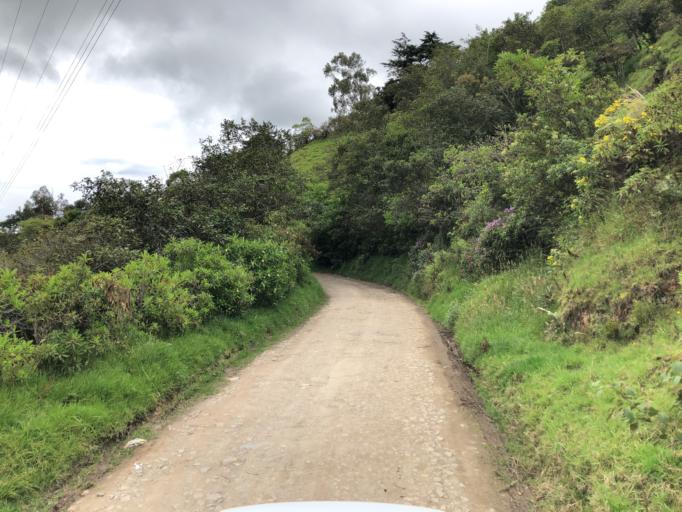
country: CO
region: Cauca
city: Totoro
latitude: 2.5101
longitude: -76.3689
